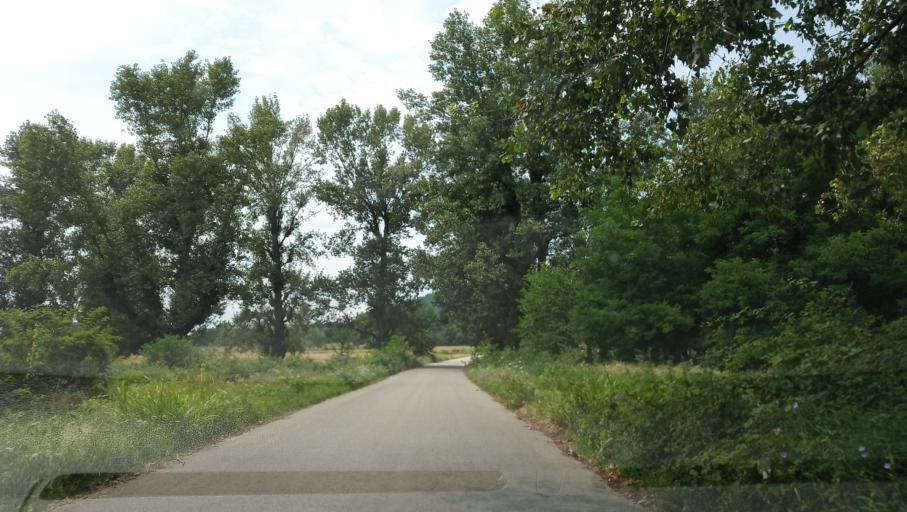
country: RO
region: Gorj
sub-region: Comuna Bumbesti-Jiu
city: Bumbesti-Jiu
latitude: 45.1626
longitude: 23.3547
